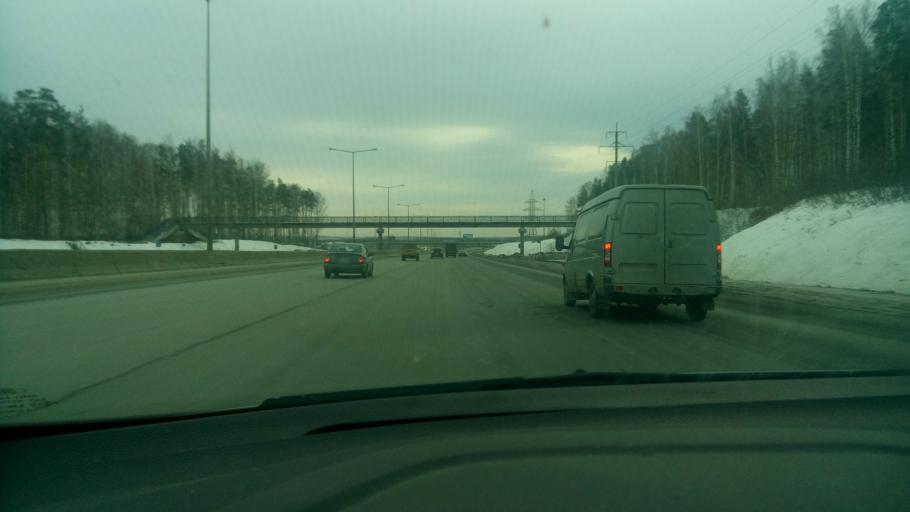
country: RU
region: Sverdlovsk
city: Istok
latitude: 56.7703
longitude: 60.7298
